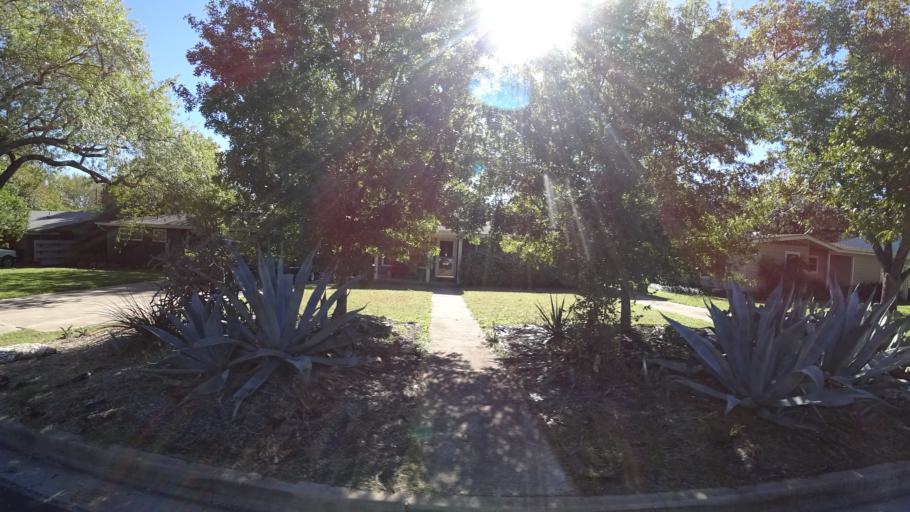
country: US
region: Texas
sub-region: Travis County
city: Austin
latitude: 30.3326
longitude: -97.7375
